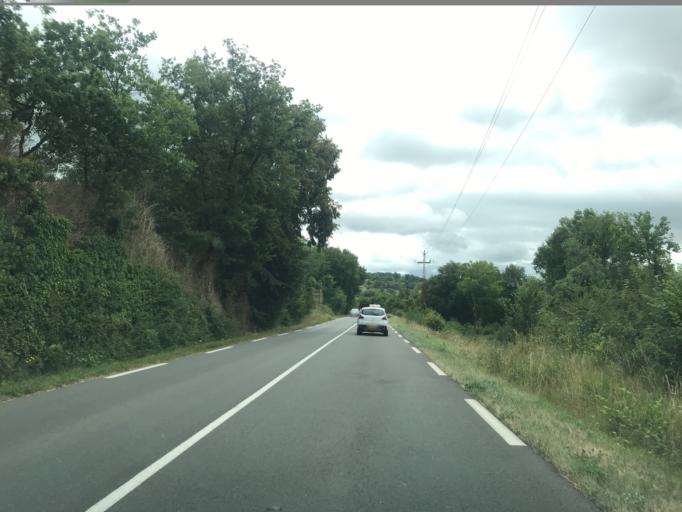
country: FR
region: Aquitaine
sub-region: Departement de la Dordogne
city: Mareuil
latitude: 45.4836
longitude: 0.3685
